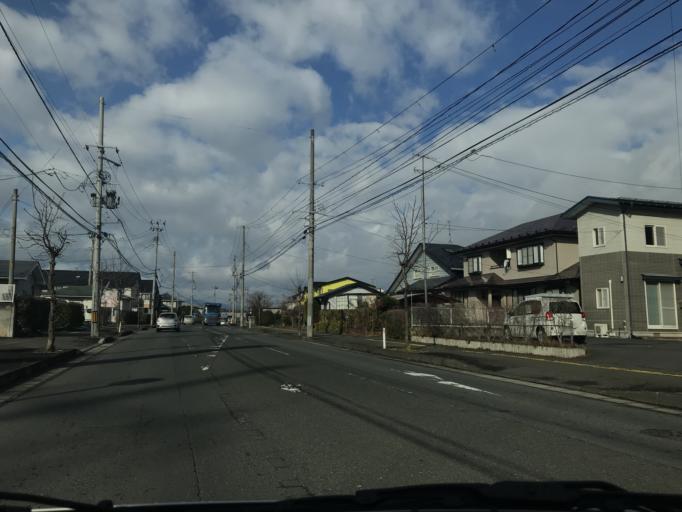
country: JP
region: Iwate
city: Mizusawa
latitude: 39.1221
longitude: 141.1322
